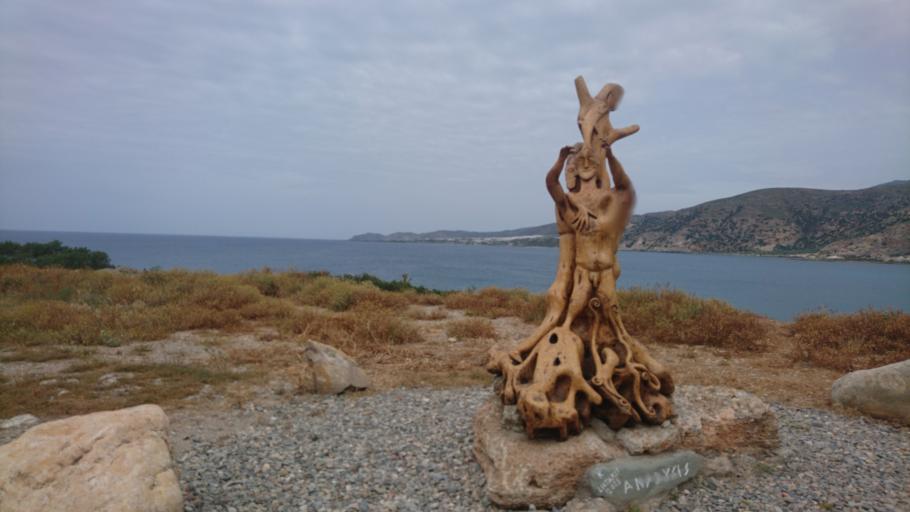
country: GR
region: Crete
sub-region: Nomos Chanias
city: Palaiochora
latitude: 35.2278
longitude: 23.6786
